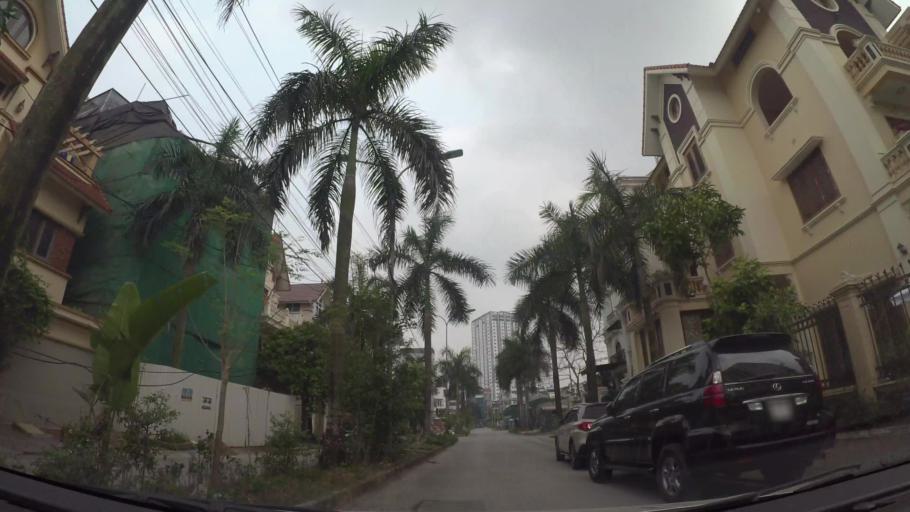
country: VN
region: Ha Noi
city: Ha Dong
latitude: 20.9824
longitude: 105.7669
